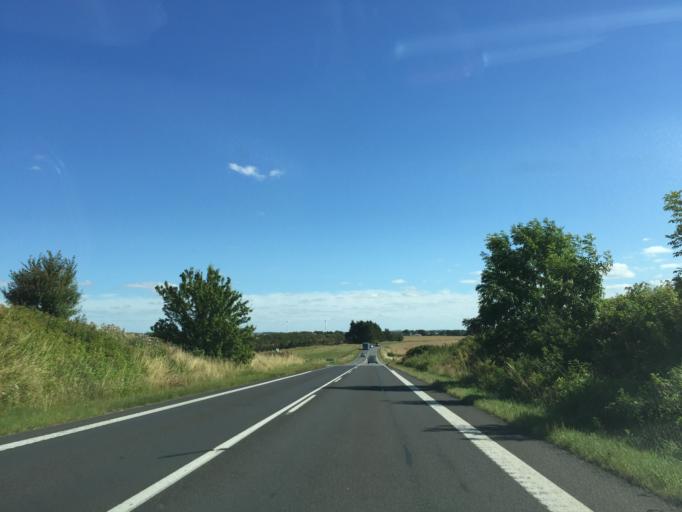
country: DK
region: Central Jutland
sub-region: Viborg Kommune
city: Bjerringbro
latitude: 56.3517
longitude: 9.6781
